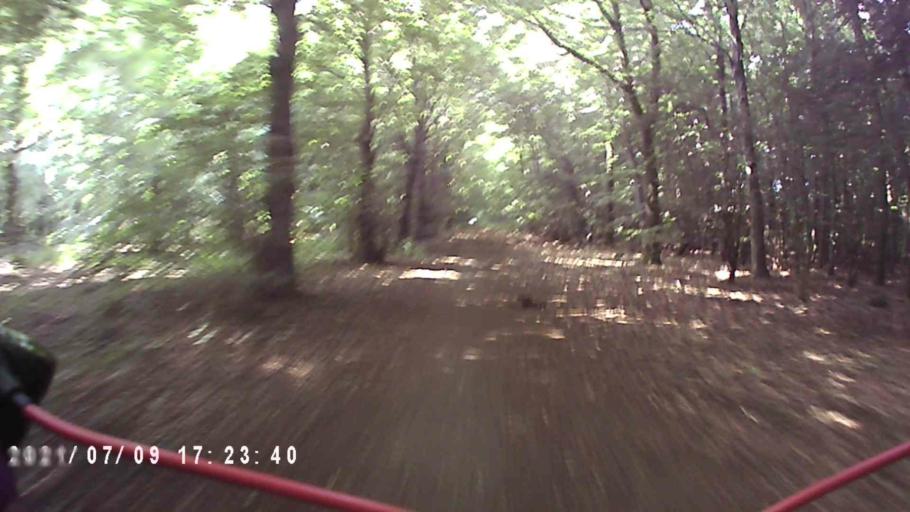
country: NL
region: Groningen
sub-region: Gemeente Vlagtwedde
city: Vlagtwedde
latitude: 53.0861
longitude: 7.1537
